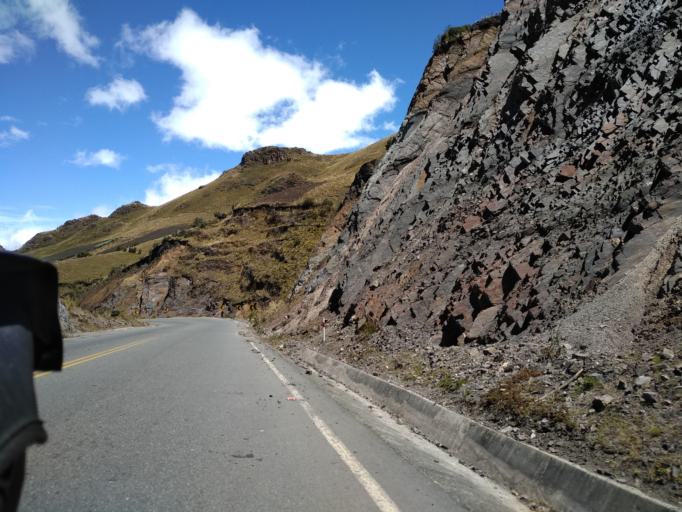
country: EC
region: Cotopaxi
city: Pujili
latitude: -0.9862
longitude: -78.9499
